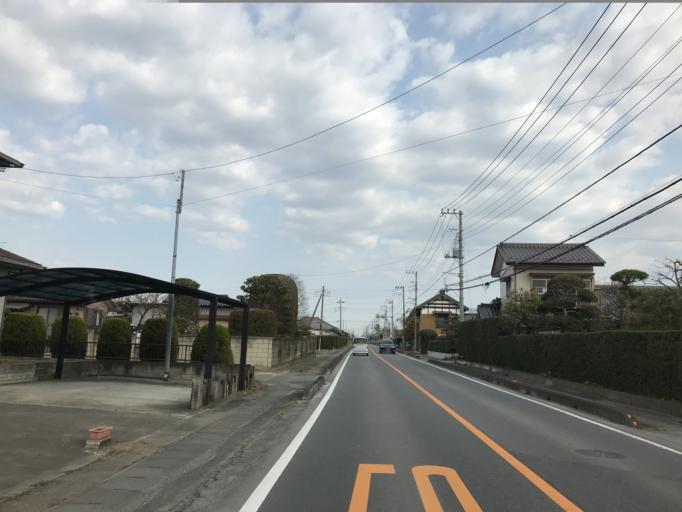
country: JP
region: Ibaraki
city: Mitsukaido
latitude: 35.9975
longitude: 140.0158
